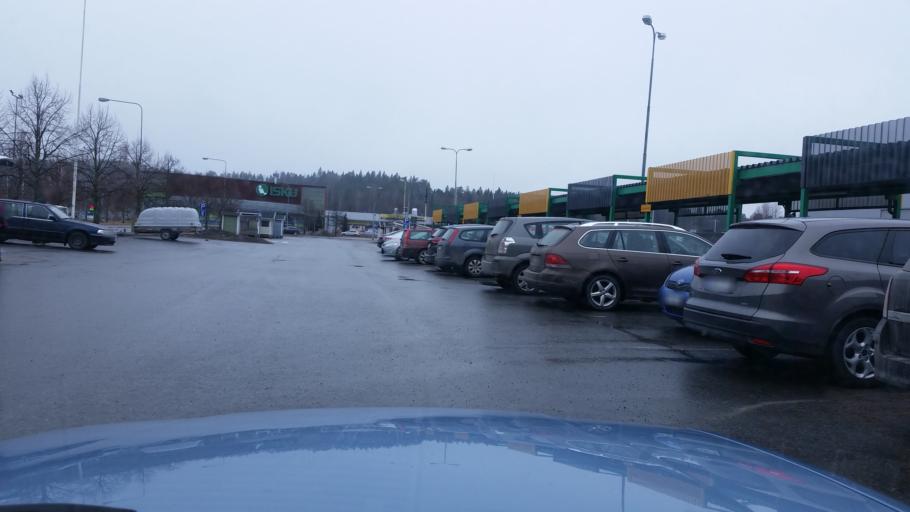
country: FI
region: Haeme
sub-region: Haemeenlinna
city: Haemeenlinna
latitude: 61.0092
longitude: 24.4192
